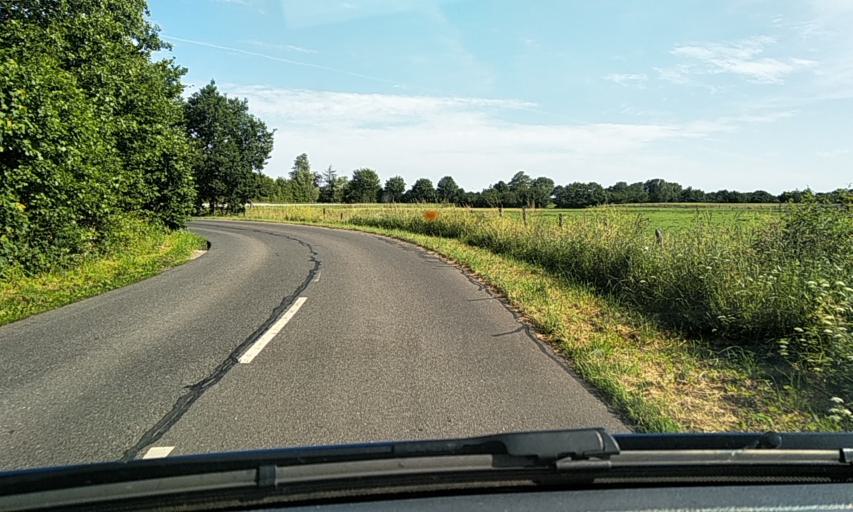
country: DE
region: Schleswig-Holstein
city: Fockbek
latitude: 54.2790
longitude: 9.5739
